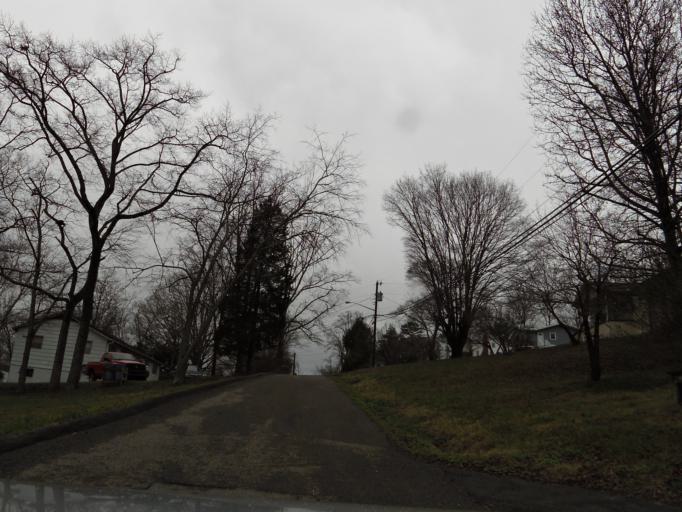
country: US
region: Tennessee
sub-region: Knox County
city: Knoxville
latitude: 35.9852
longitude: -84.0256
